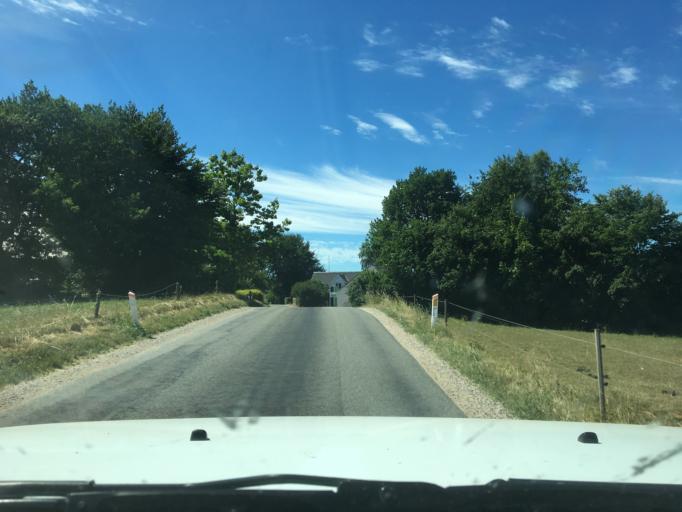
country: DK
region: Central Jutland
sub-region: Syddjurs Kommune
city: Ronde
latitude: 56.3424
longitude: 10.4364
